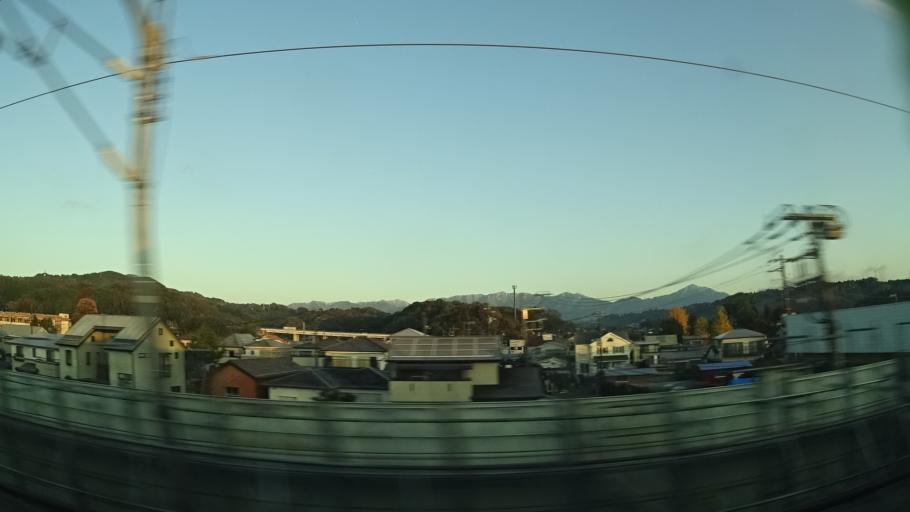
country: JP
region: Kanagawa
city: Ninomiya
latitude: 35.3012
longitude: 139.2281
